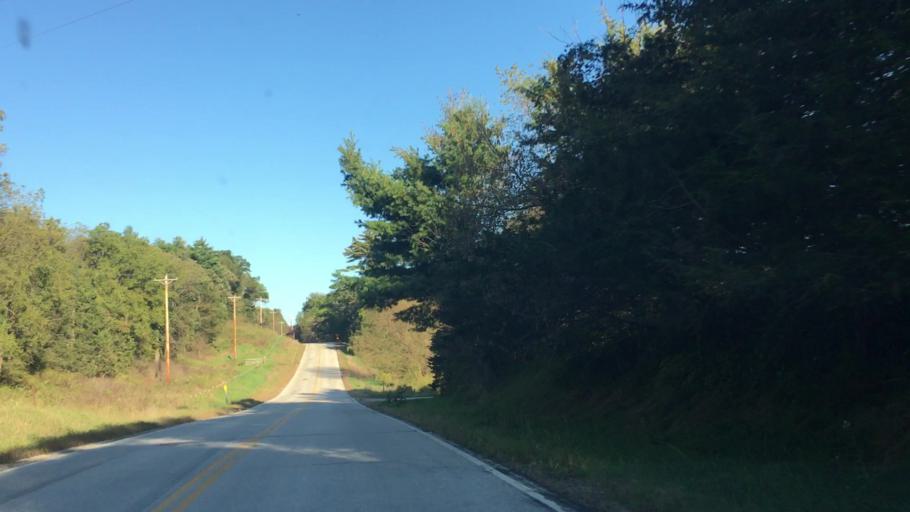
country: US
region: Minnesota
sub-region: Fillmore County
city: Chatfield
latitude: 43.8181
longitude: -92.0469
